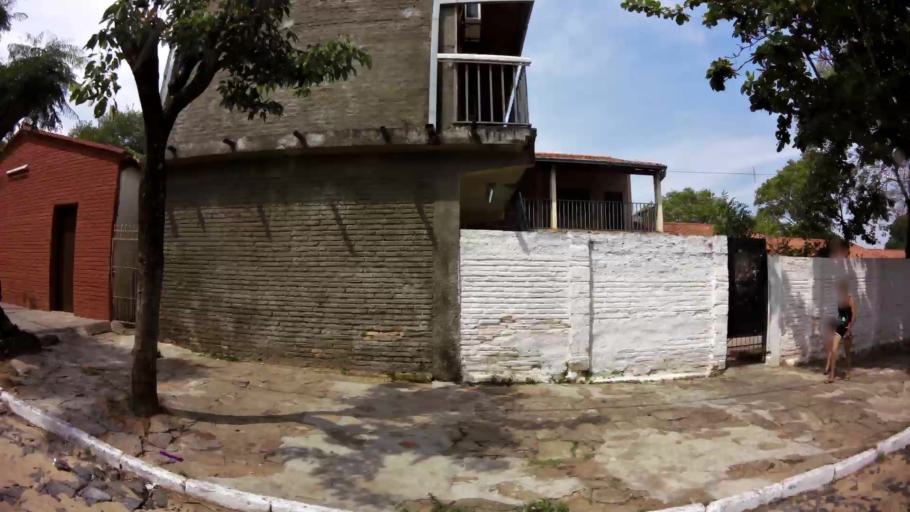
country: PY
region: Asuncion
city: Asuncion
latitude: -25.2640
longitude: -57.5850
